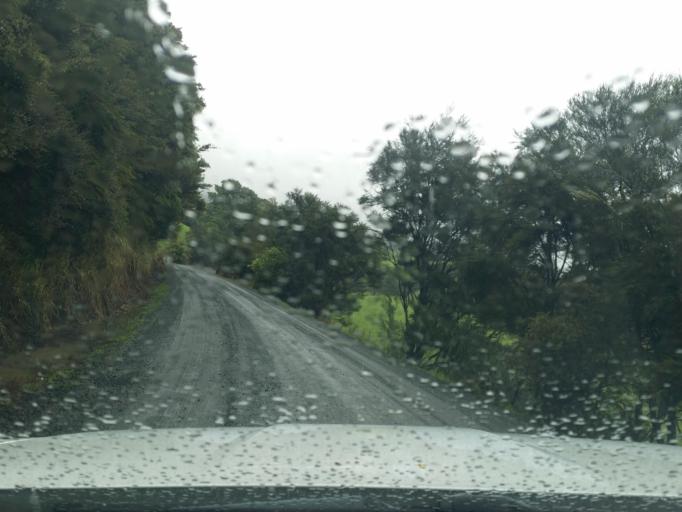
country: NZ
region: Northland
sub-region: Kaipara District
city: Dargaville
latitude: -35.7811
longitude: 173.9540
